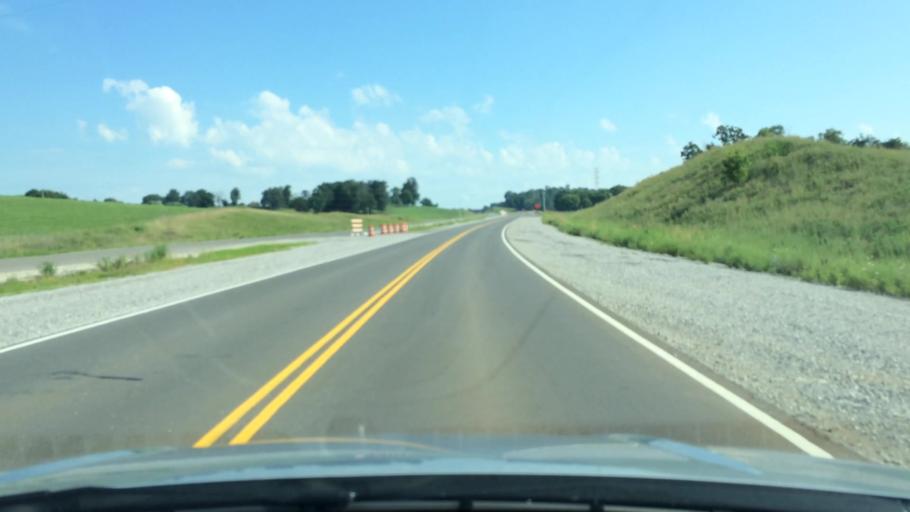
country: US
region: Tennessee
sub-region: Jefferson County
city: White Pine
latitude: 36.1442
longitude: -83.3433
